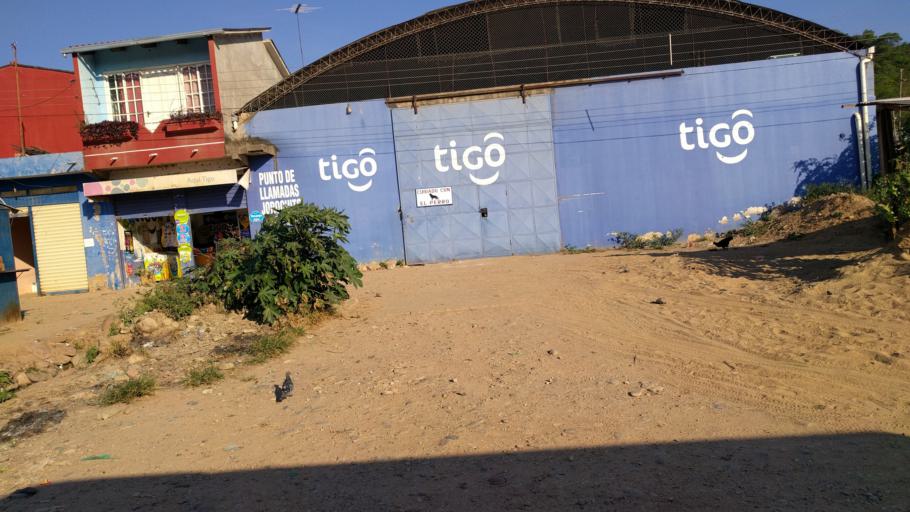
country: BO
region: Santa Cruz
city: Jorochito
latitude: -18.0567
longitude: -63.4285
